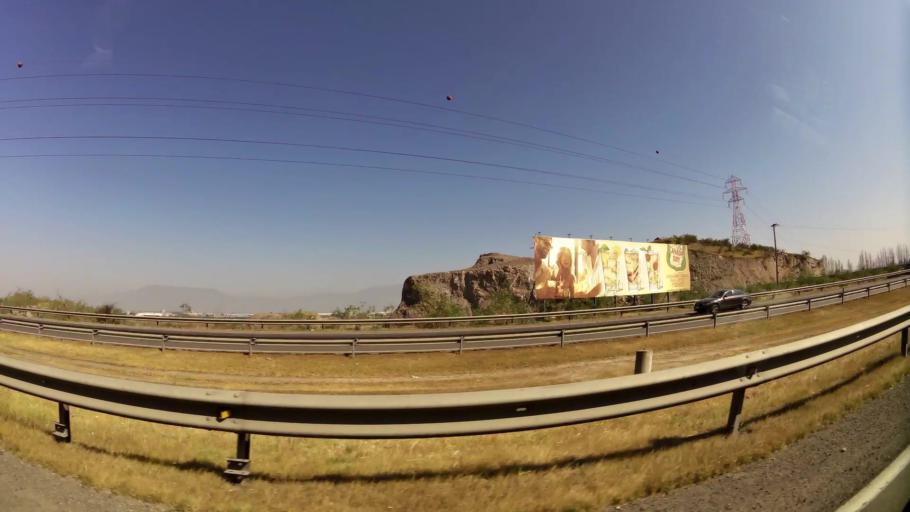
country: CL
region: Santiago Metropolitan
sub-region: Provincia de Chacabuco
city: Chicureo Abajo
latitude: -33.3181
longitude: -70.7069
